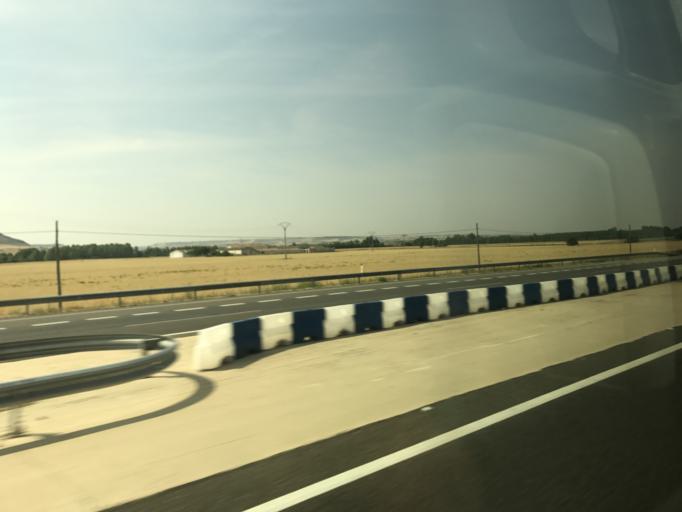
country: ES
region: Castille and Leon
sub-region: Provincia de Palencia
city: Palenzuela
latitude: 42.1221
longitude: -4.1464
